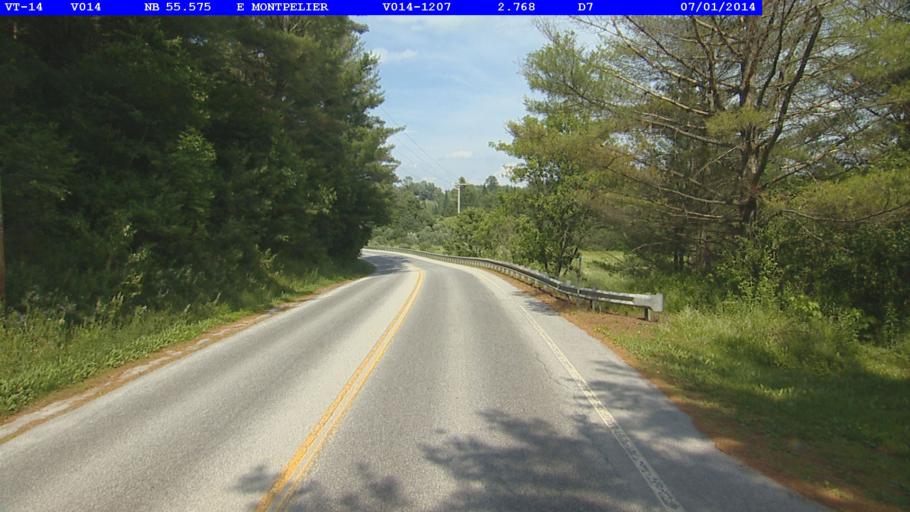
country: US
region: Vermont
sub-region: Washington County
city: Barre
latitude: 44.2742
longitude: -72.4817
